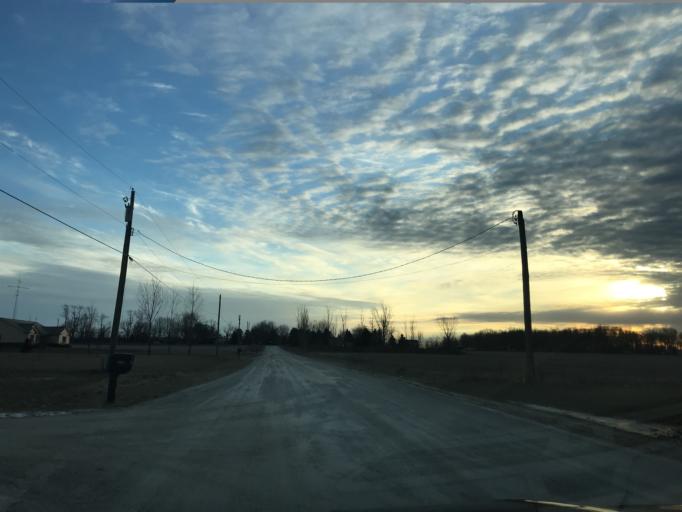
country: US
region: Michigan
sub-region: Macomb County
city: Armada
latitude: 42.9014
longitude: -82.8873
